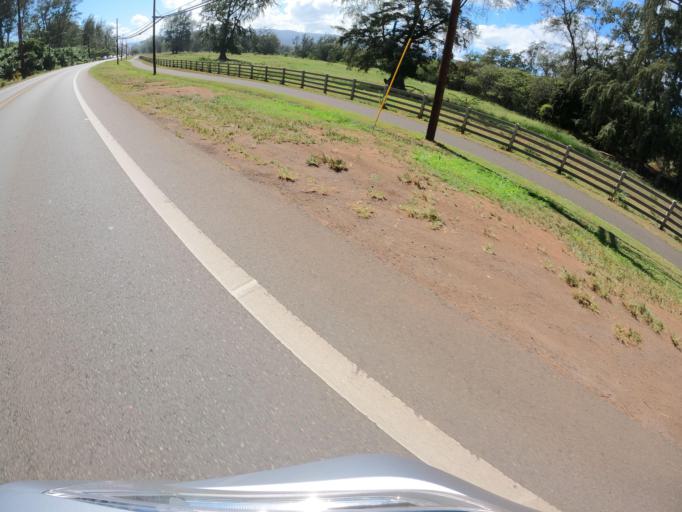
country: US
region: Hawaii
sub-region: Honolulu County
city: Kahuku
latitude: 21.6711
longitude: -157.9397
